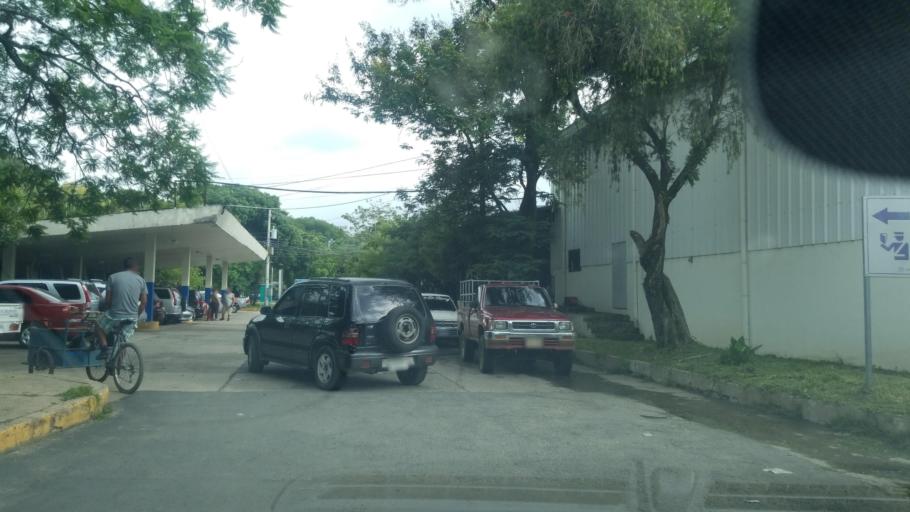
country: HN
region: Ocotepeque
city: Antigua Ocotepeque
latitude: 14.3730
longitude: -89.2097
